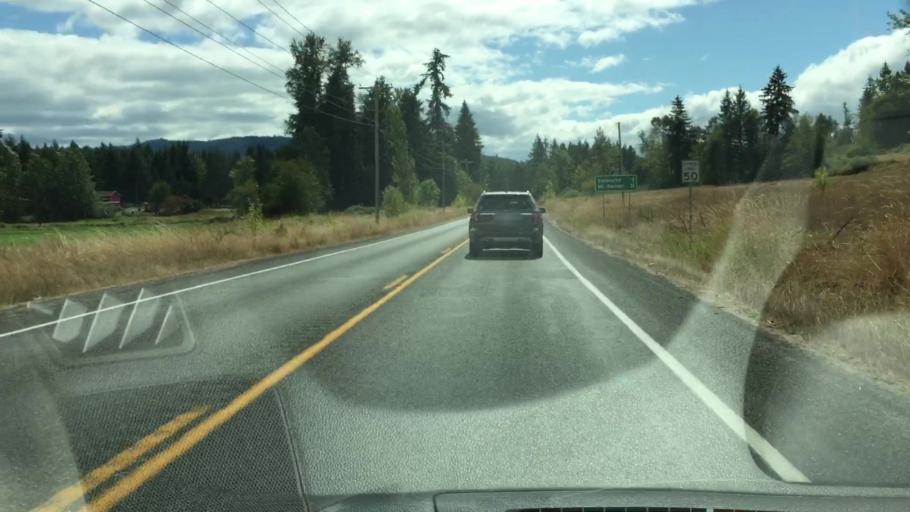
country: US
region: Washington
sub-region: Pierce County
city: Eatonville
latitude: 46.8837
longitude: -122.3008
